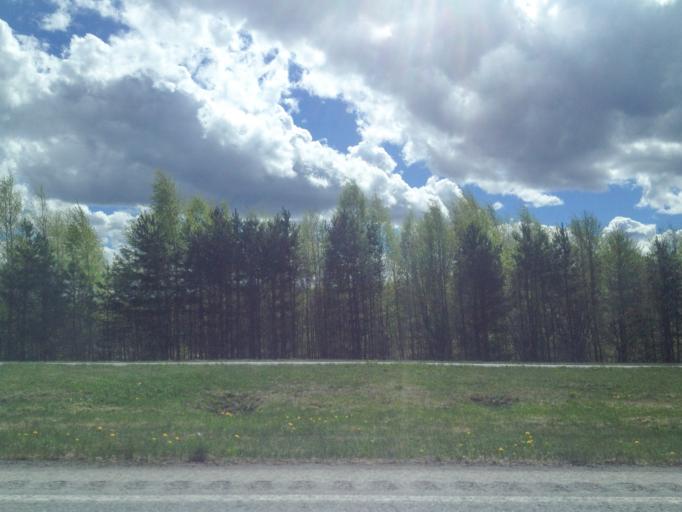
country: FI
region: Haeme
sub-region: Haemeenlinna
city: Parola
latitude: 61.0803
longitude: 24.2598
